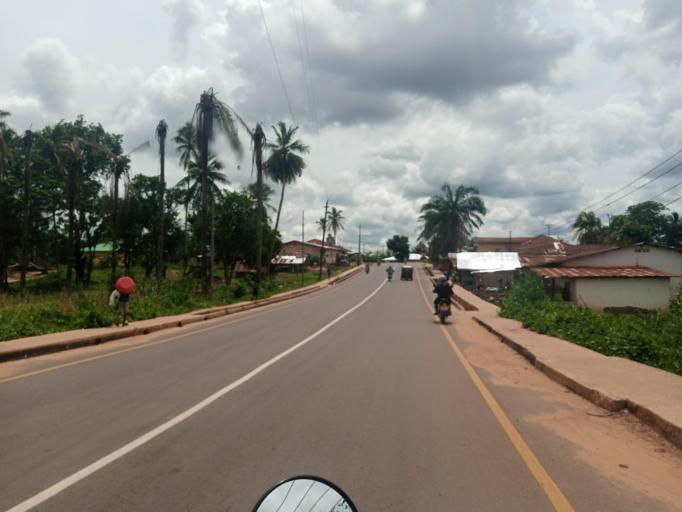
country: SL
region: Southern Province
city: Bo
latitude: 7.9552
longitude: -11.7203
